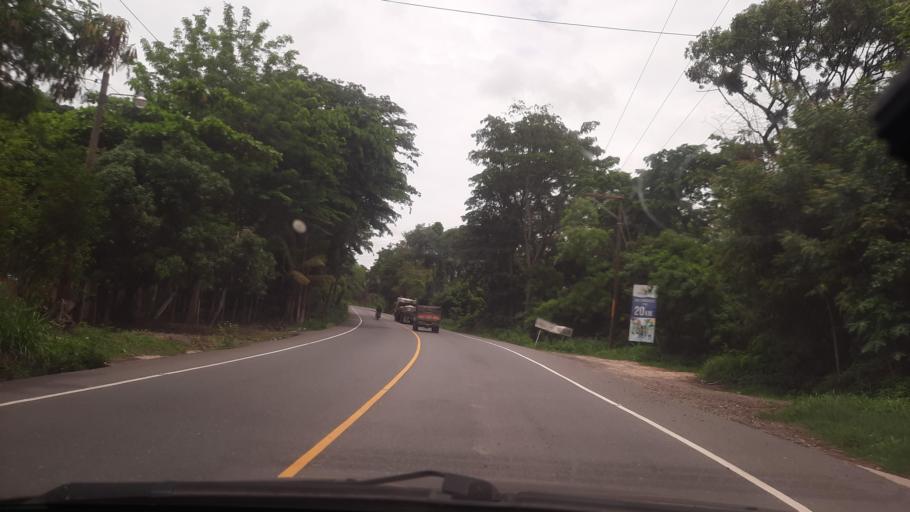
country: GT
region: Zacapa
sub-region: Municipio de Zacapa
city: Gualan
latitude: 15.1485
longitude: -89.3265
